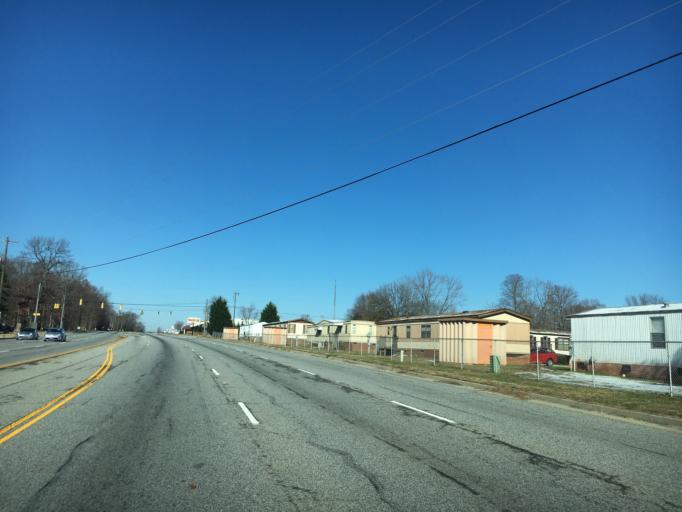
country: US
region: South Carolina
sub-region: Greenville County
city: Greer
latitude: 34.9008
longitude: -82.2366
